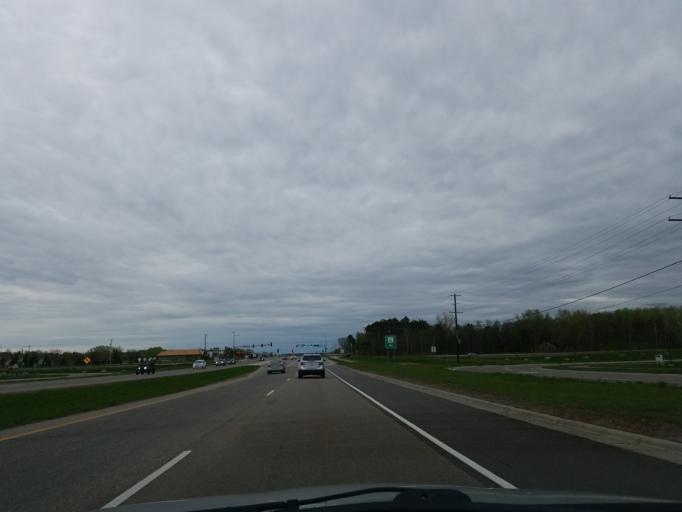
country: US
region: Minnesota
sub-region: Washington County
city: Stillwater
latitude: 45.0359
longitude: -92.8244
